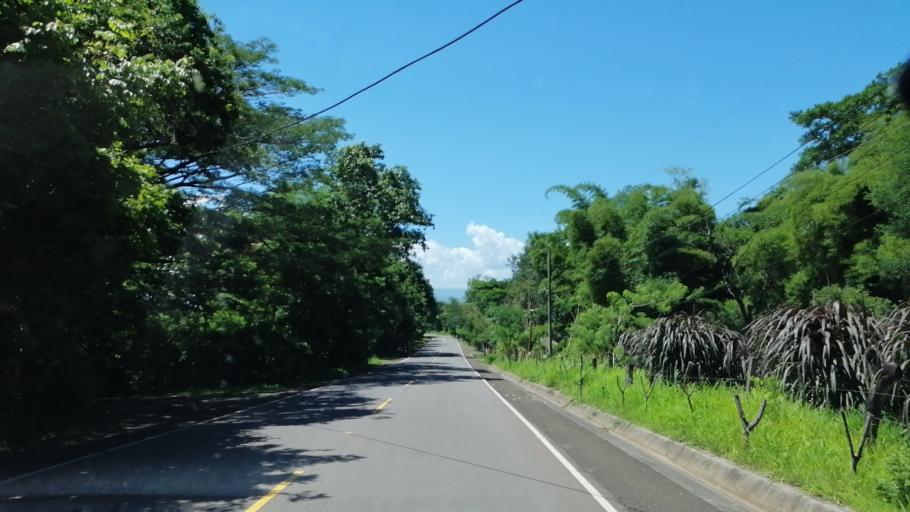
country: SV
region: San Miguel
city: Ciudad Barrios
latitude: 13.8119
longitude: -88.1882
